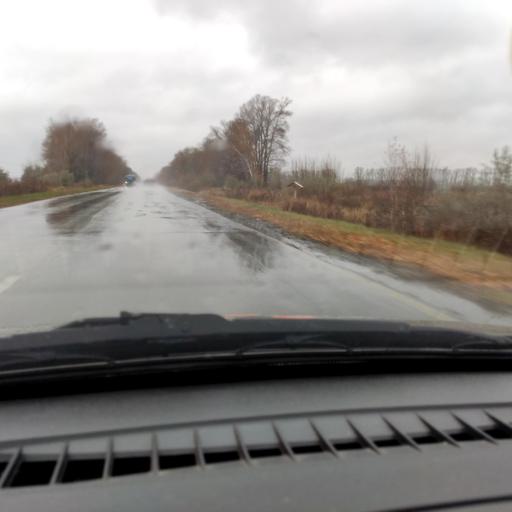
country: RU
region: Samara
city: Tol'yatti
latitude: 53.6613
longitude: 49.2842
